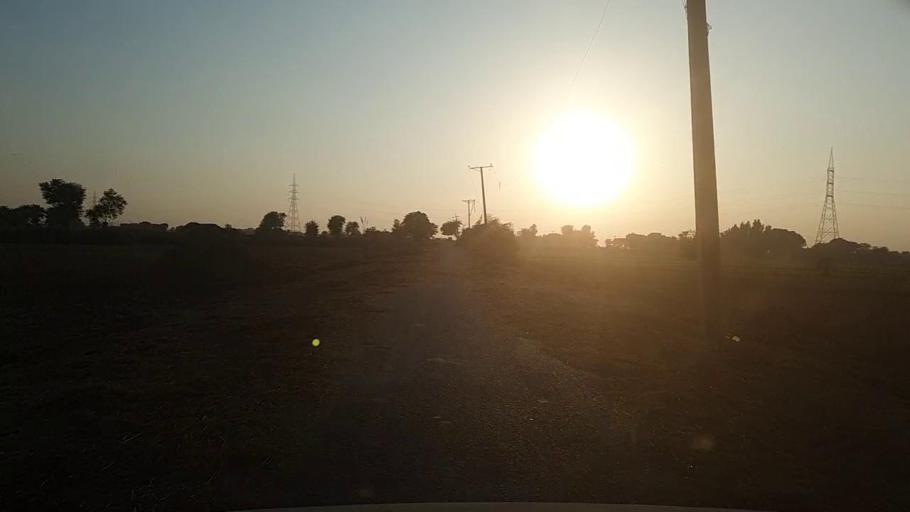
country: PK
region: Sindh
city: Mehar
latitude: 27.1883
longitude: 67.7427
